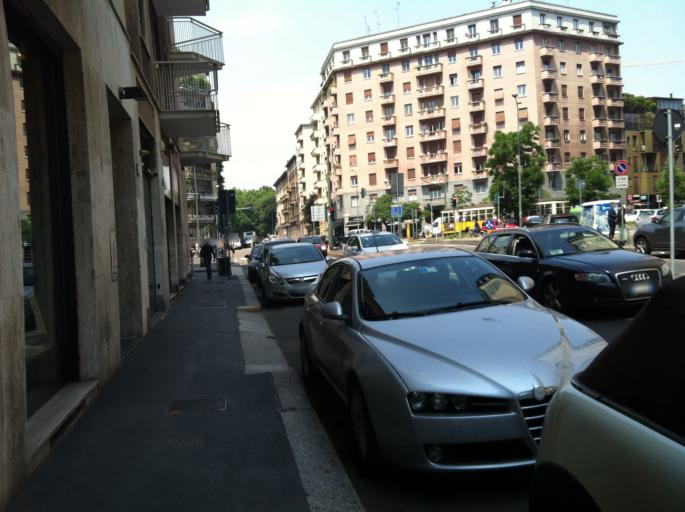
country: IT
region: Lombardy
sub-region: Citta metropolitana di Milano
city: Milano
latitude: 45.4740
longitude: 9.2111
